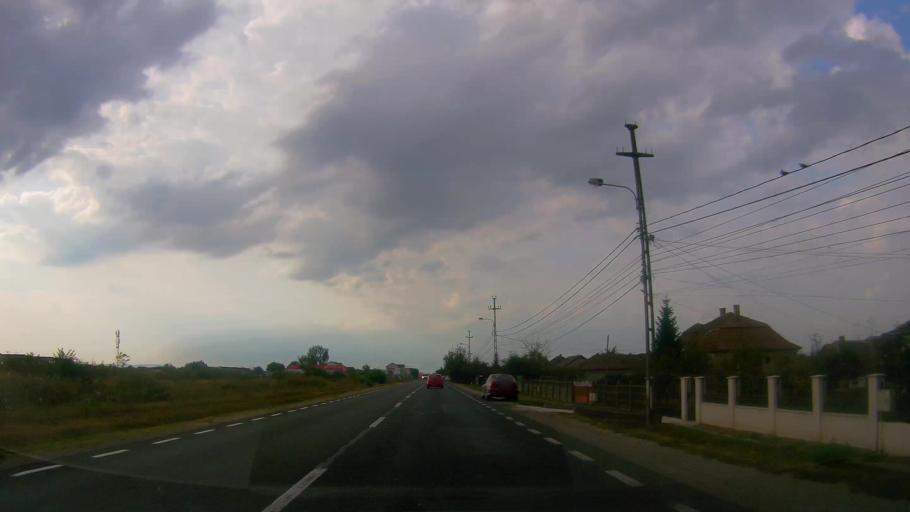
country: RO
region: Satu Mare
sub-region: Municipiul Satu Mare
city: Satu Mare
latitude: 47.7592
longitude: 22.8832
